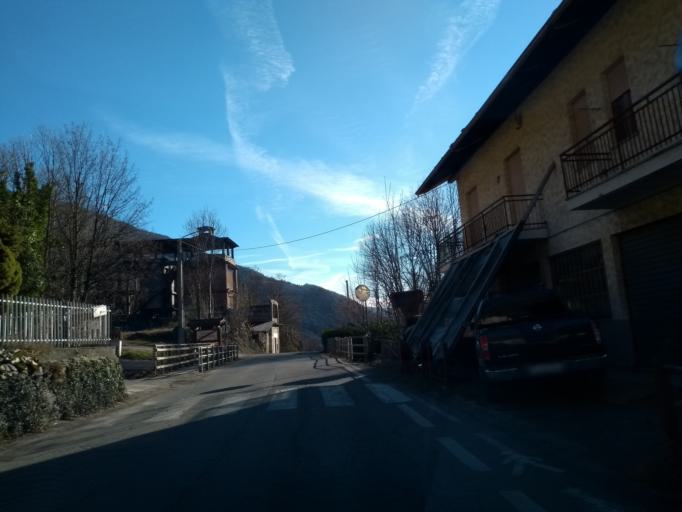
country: IT
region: Piedmont
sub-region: Provincia di Torino
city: Cantoira
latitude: 45.3359
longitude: 7.3878
